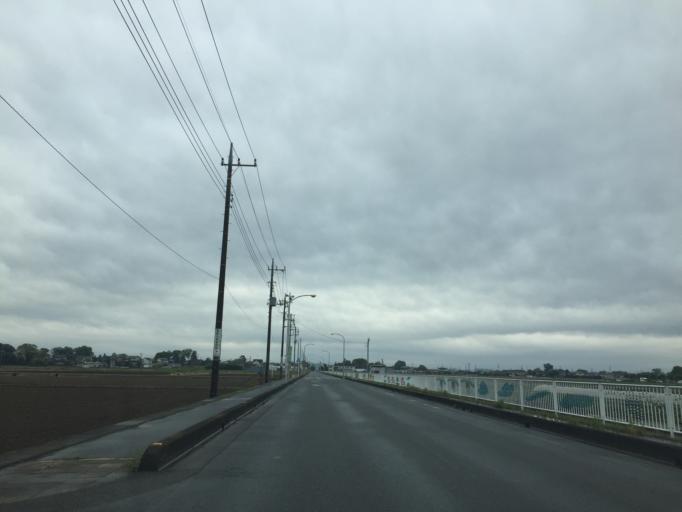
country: JP
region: Saitama
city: Shiki
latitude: 35.8693
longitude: 139.5653
